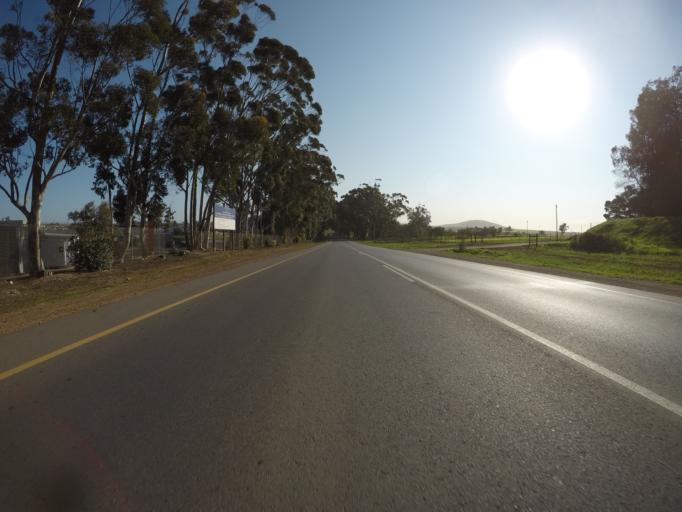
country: ZA
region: Western Cape
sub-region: City of Cape Town
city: Kraaifontein
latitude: -33.7788
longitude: 18.7221
